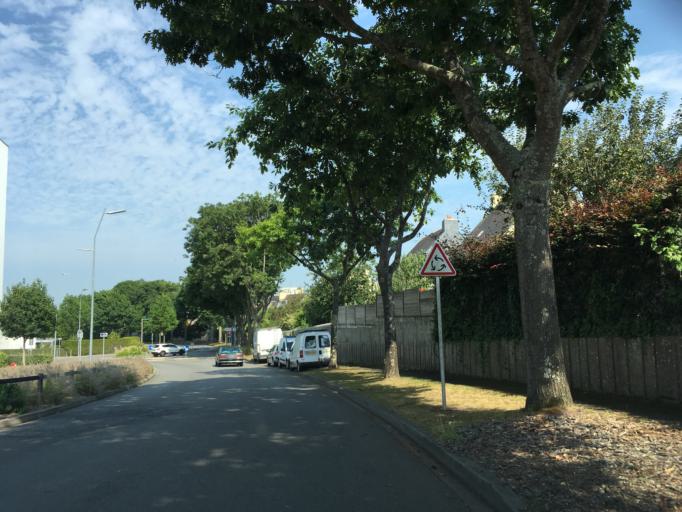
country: FR
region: Brittany
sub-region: Departement du Morbihan
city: Lorient
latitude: 47.7616
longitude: -3.3771
